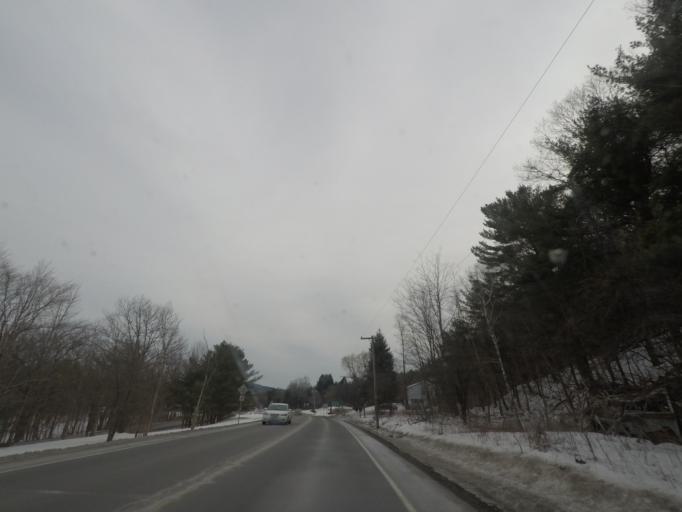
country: US
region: New York
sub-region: Albany County
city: Voorheesville
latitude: 42.5943
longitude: -73.9874
